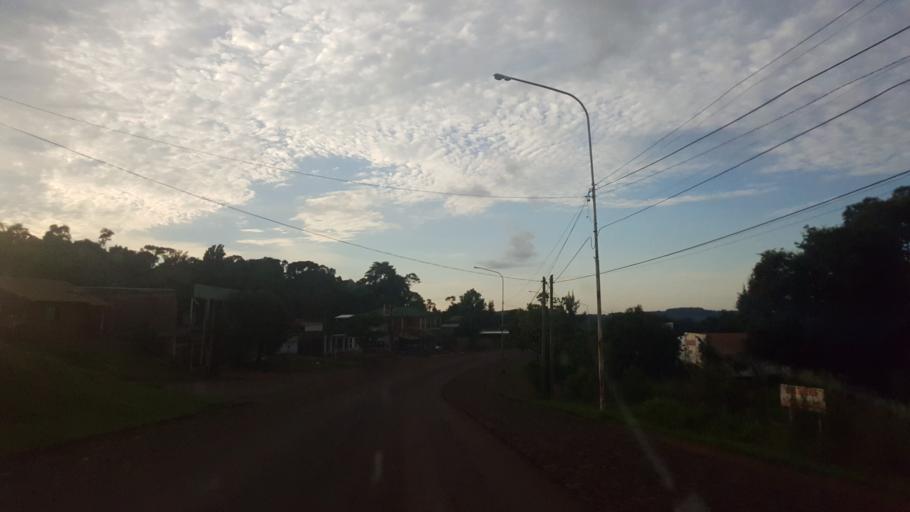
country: AR
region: Misiones
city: Dos de Mayo
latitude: -27.0304
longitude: -54.6865
